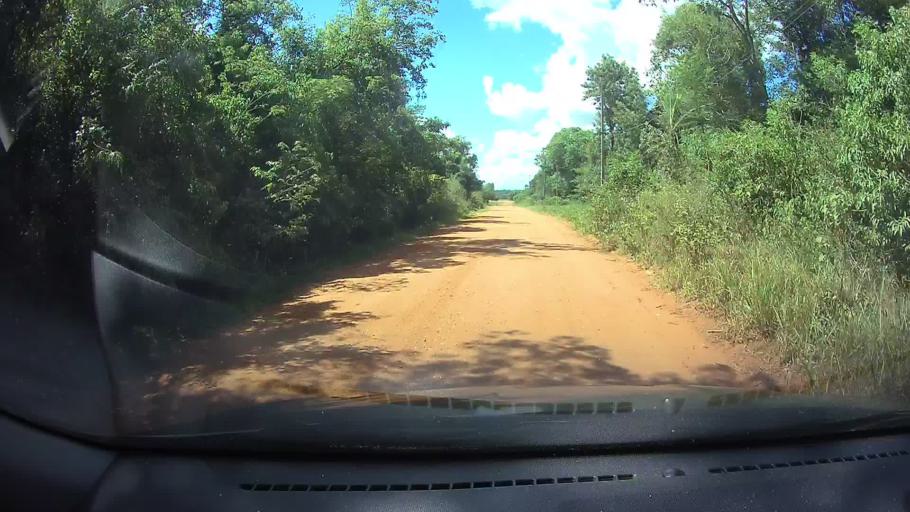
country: PY
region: Paraguari
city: La Colmena
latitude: -25.9007
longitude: -56.7929
